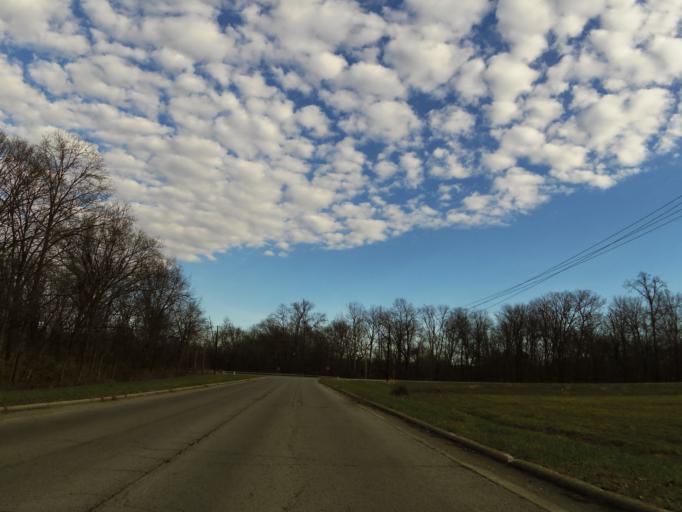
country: US
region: Illinois
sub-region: Jefferson County
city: Mount Vernon
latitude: 38.3546
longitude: -88.9690
